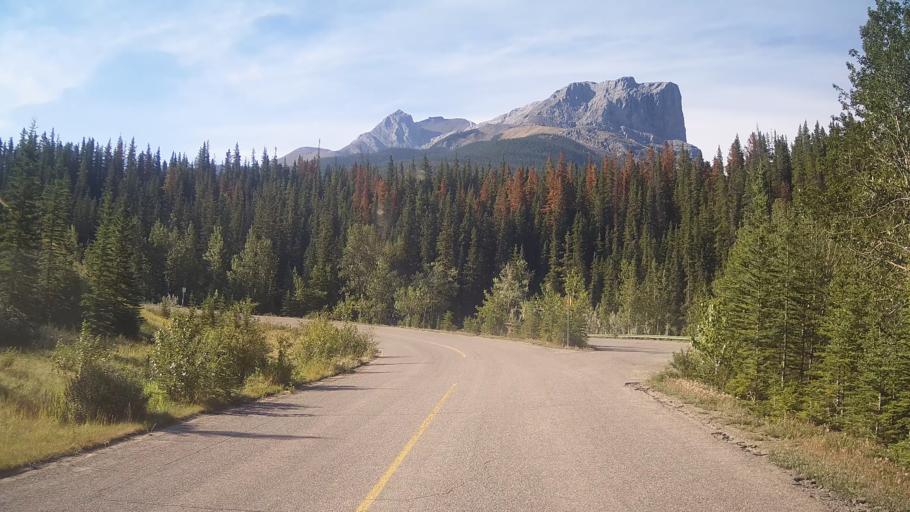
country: CA
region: Alberta
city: Jasper Park Lodge
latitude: 53.2000
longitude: -117.9225
